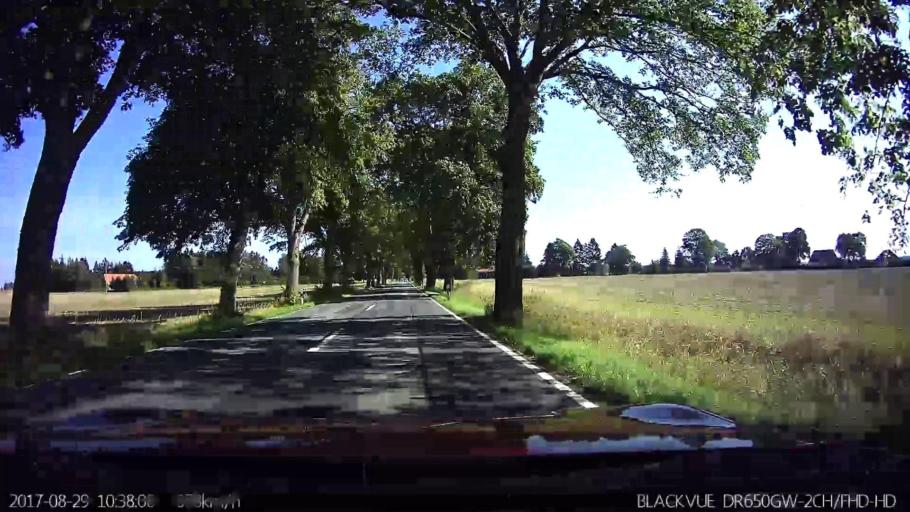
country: DE
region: Mecklenburg-Vorpommern
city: Franzburg
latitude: 54.1629
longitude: 12.8093
